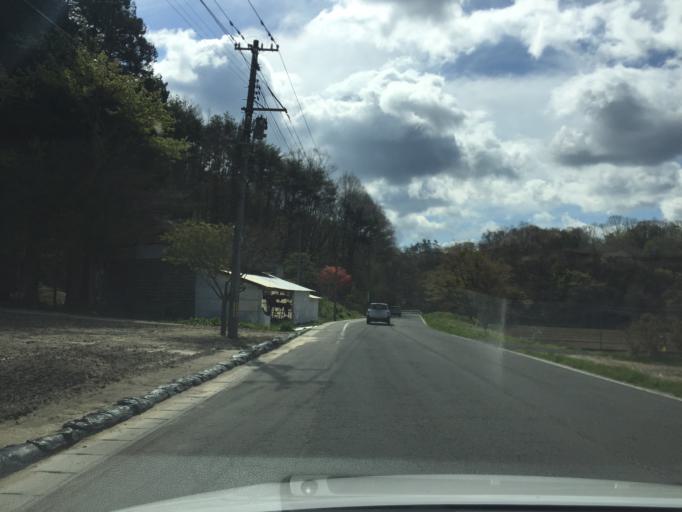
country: JP
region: Fukushima
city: Funehikimachi-funehiki
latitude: 37.5950
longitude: 140.6833
